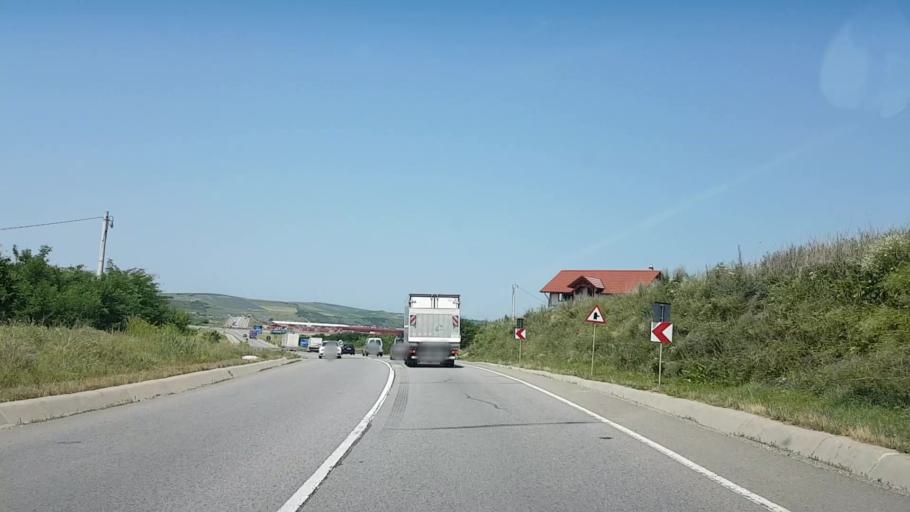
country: RO
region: Cluj
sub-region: Comuna Apahida
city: Dezmir
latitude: 46.7727
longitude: 23.7014
